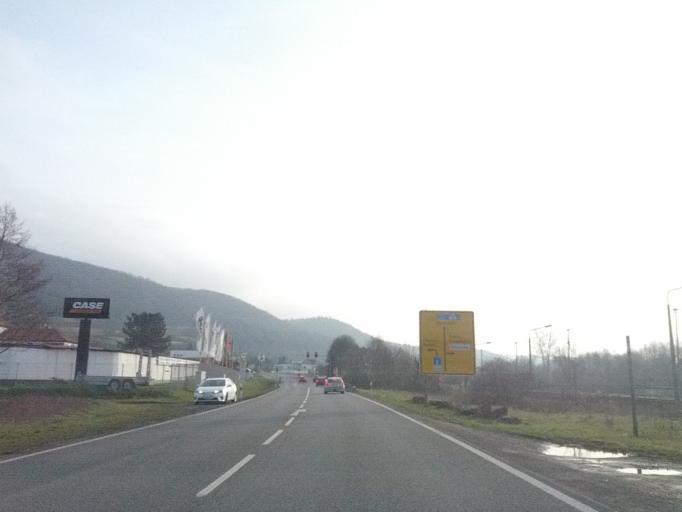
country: DE
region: Thuringia
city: Walldorf
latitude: 50.6190
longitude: 10.3884
